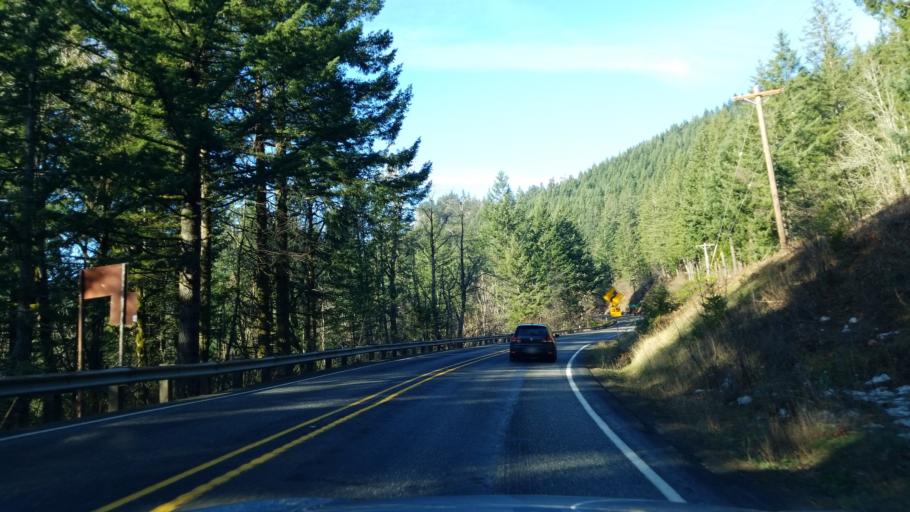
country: US
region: Oregon
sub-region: Hood River County
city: Cascade Locks
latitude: 45.6308
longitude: -122.0112
